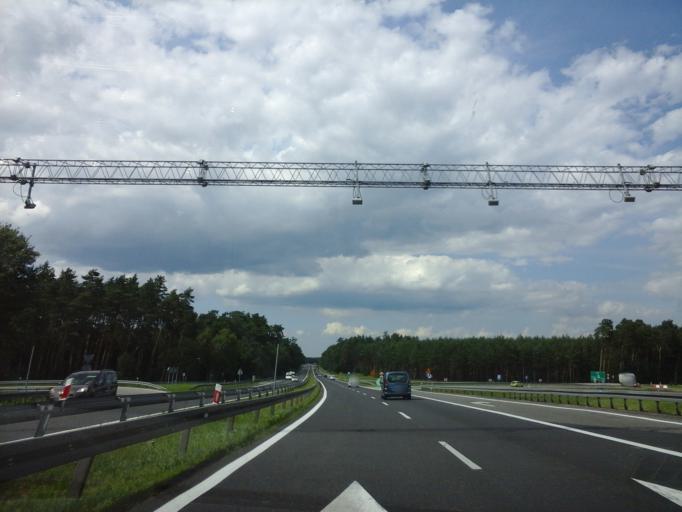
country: PL
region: West Pomeranian Voivodeship
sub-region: Powiat goleniowski
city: Goleniow
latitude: 53.5333
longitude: 14.8107
